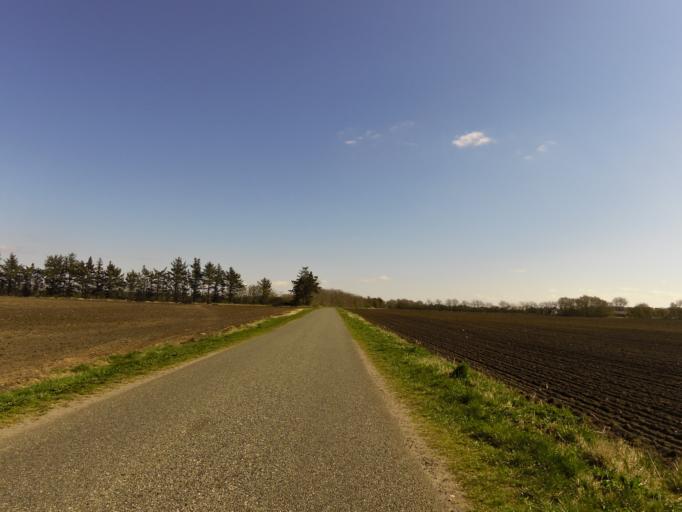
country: DK
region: South Denmark
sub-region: Esbjerg Kommune
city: Ribe
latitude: 55.3378
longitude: 8.8731
